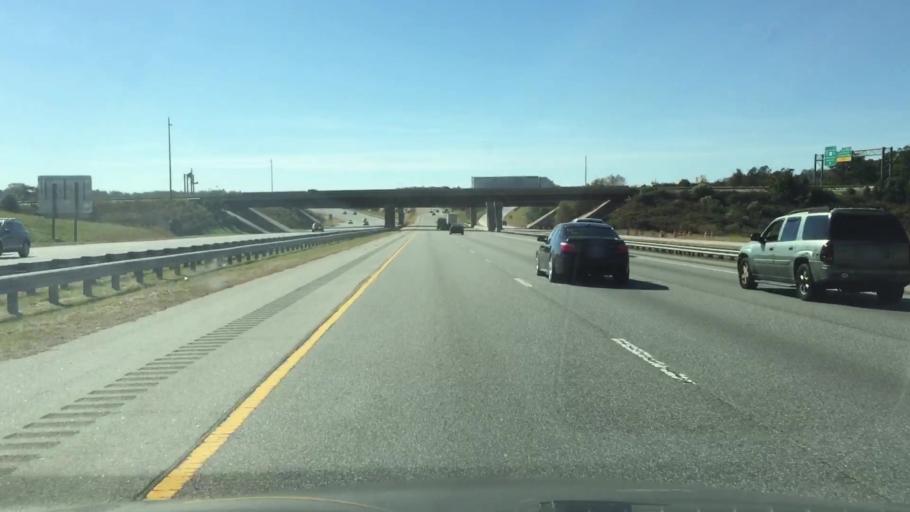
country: US
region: North Carolina
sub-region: Guilford County
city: Greensboro
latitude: 36.0068
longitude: -79.8486
